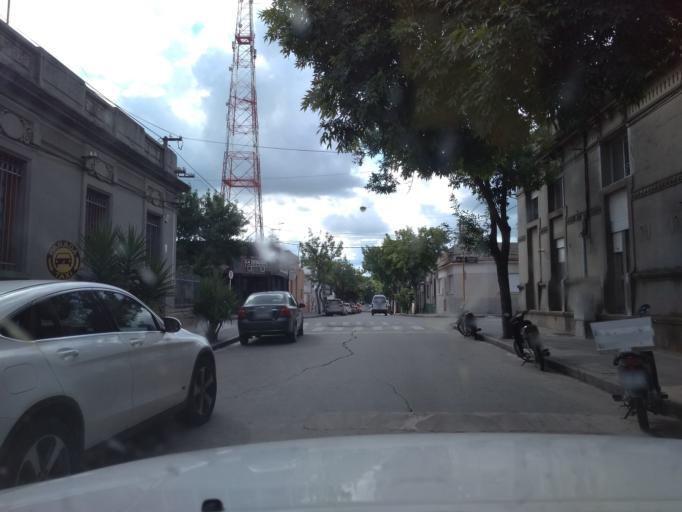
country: UY
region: Florida
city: Florida
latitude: -34.0998
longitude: -56.2123
